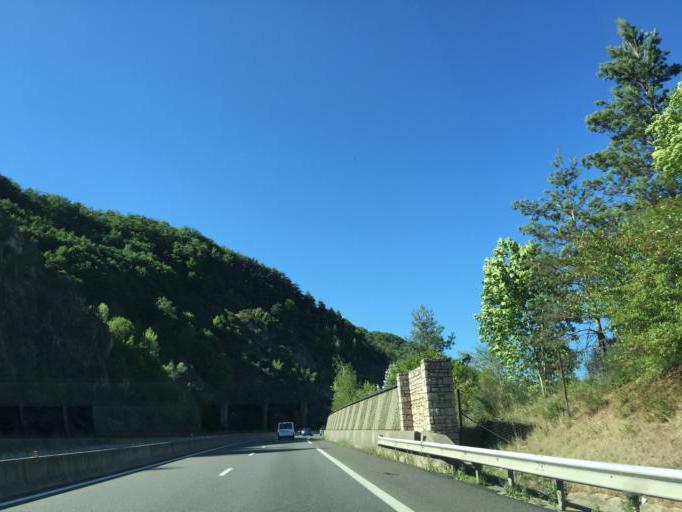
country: FR
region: Languedoc-Roussillon
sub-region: Departement de la Lozere
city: La Canourgue
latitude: 44.4522
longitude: 3.1923
